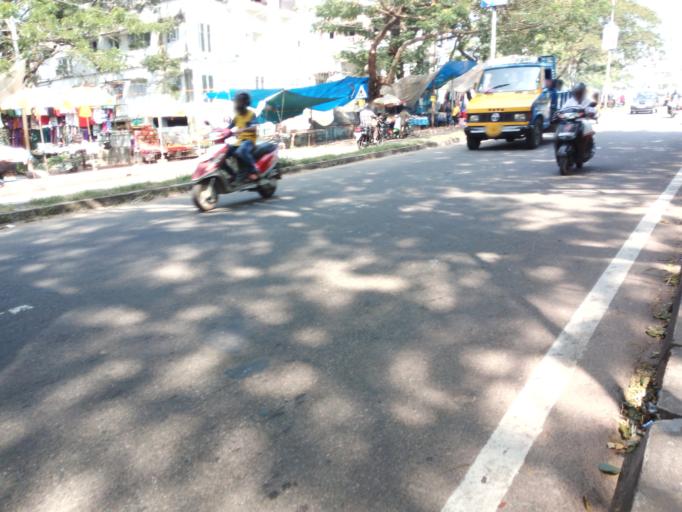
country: IN
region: Kerala
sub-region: Thrissur District
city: Trichur
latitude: 10.5181
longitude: 76.2160
